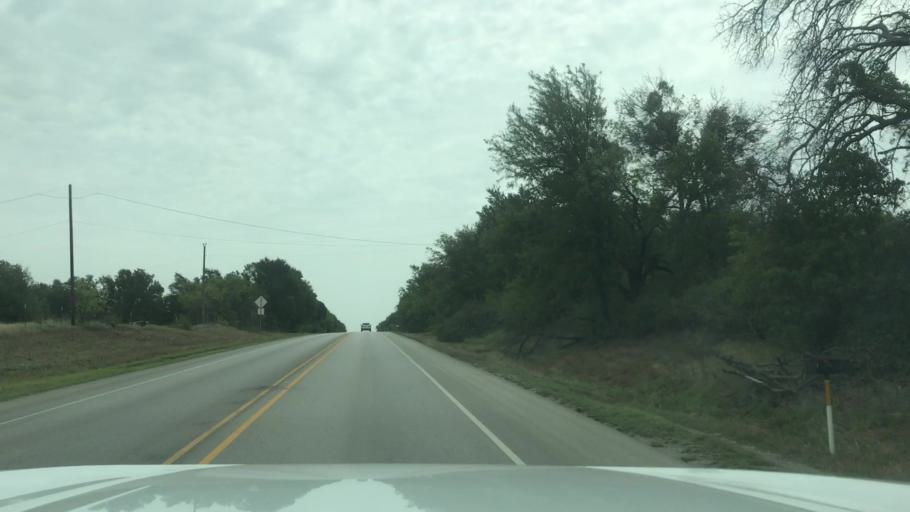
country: US
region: Texas
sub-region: Erath County
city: Dublin
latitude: 32.0985
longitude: -98.3944
